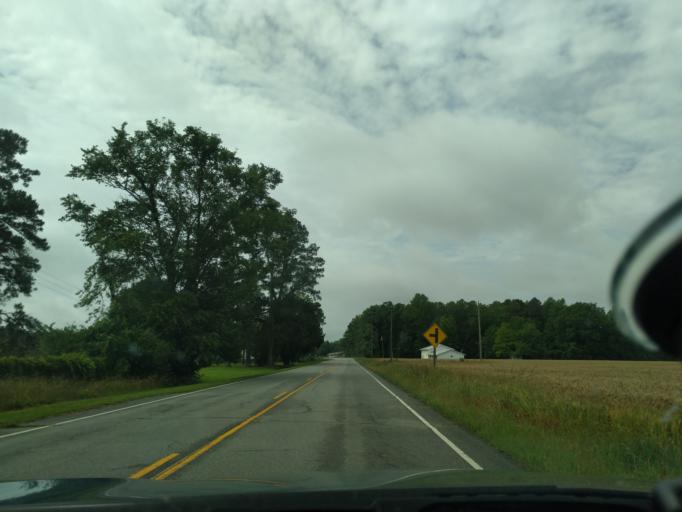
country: US
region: North Carolina
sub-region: Chowan County
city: Edenton
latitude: 35.9140
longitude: -76.6014
